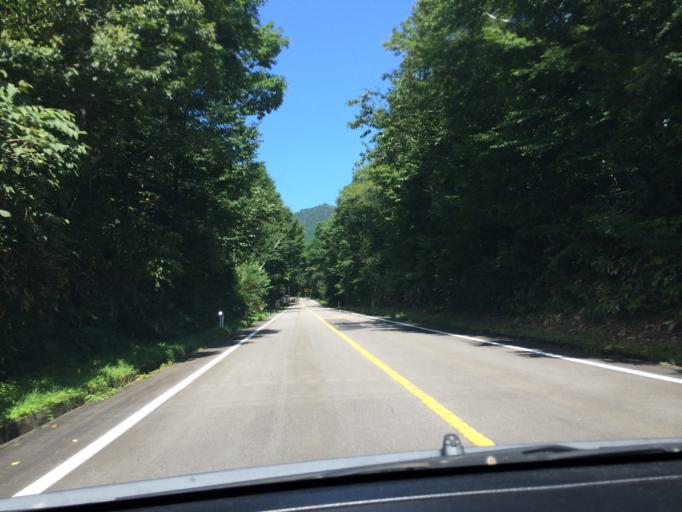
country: JP
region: Tottori
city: Kurayoshi
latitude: 35.3244
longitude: 133.6039
